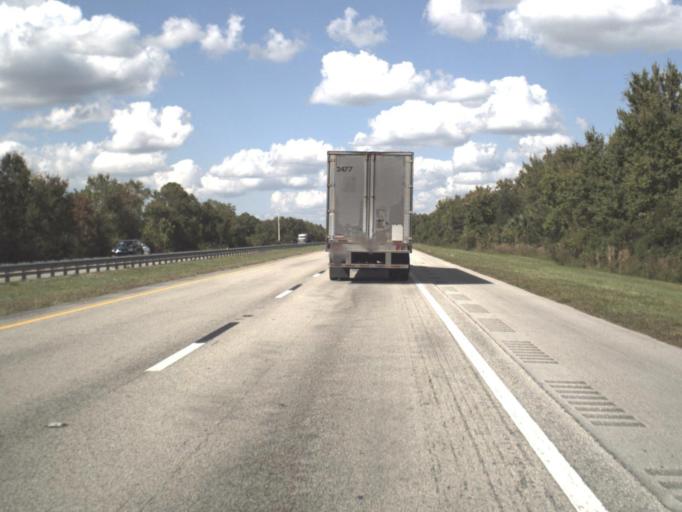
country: US
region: Florida
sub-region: Indian River County
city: Fellsmere
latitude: 27.6214
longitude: -80.8373
